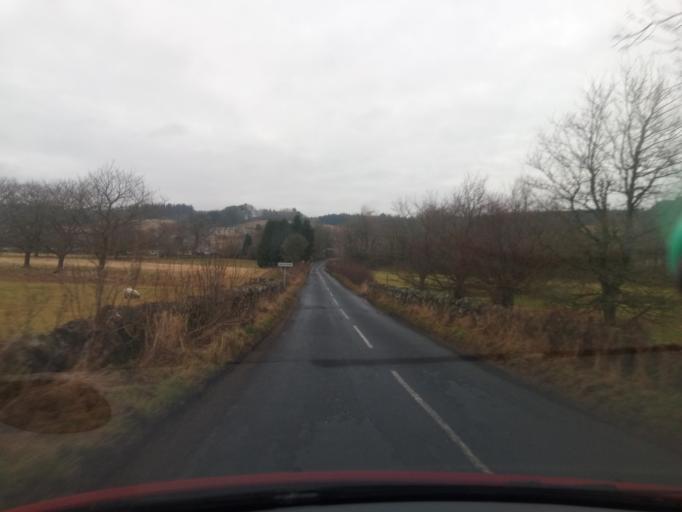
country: GB
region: England
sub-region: Northumberland
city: Rochester
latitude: 55.1783
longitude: -2.4367
